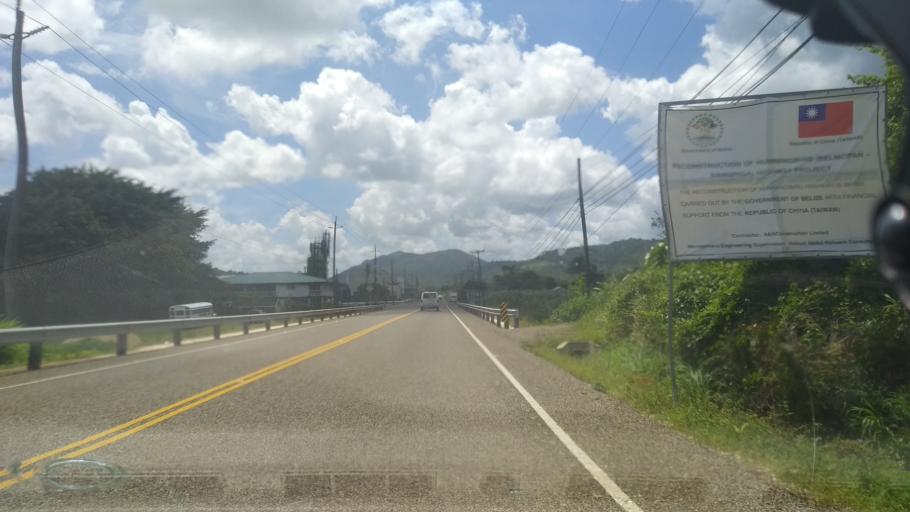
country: BZ
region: Stann Creek
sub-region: Dangriga
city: Dangriga
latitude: 16.9893
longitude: -88.4002
